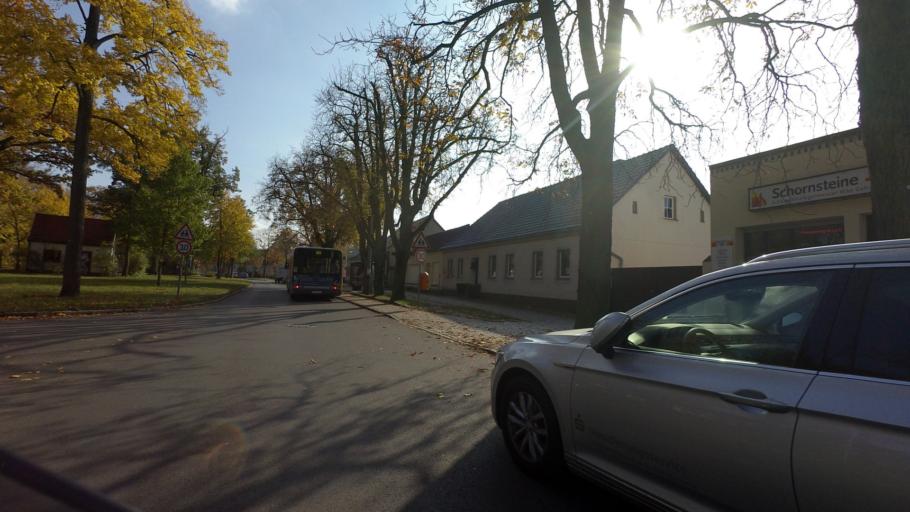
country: DE
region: Berlin
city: Muggelheim
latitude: 52.4124
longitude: 13.6615
